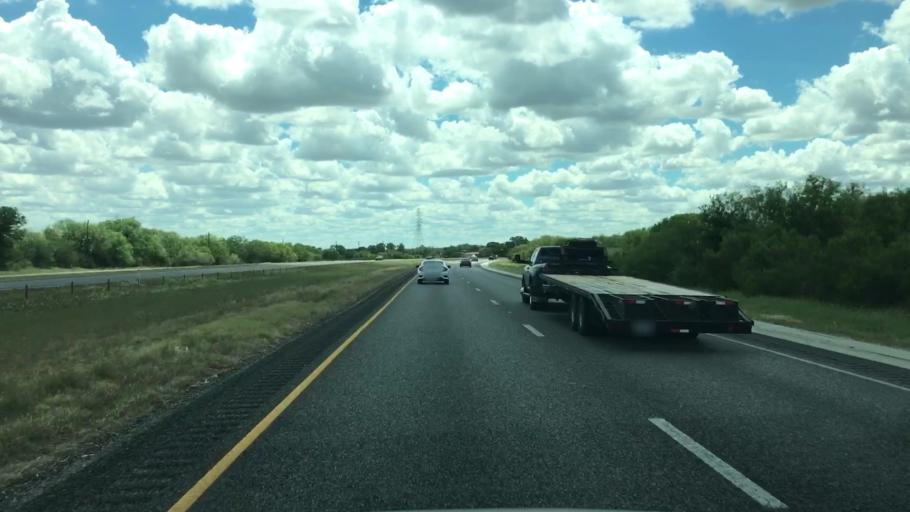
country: US
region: Texas
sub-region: Bexar County
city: Elmendorf
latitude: 29.2547
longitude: -98.3951
